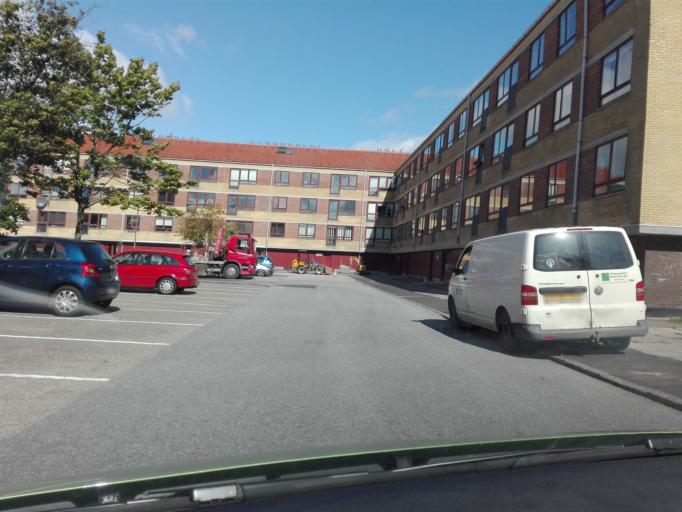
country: DK
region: Central Jutland
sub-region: Arhus Kommune
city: Arhus
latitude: 56.1204
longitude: 10.1782
